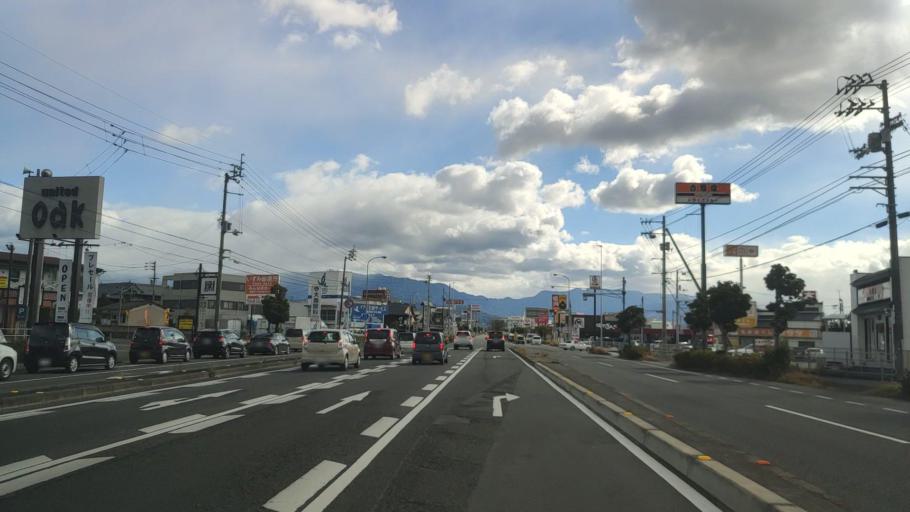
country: JP
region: Ehime
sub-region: Shikoku-chuo Shi
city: Matsuyama
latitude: 33.8152
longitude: 132.7951
